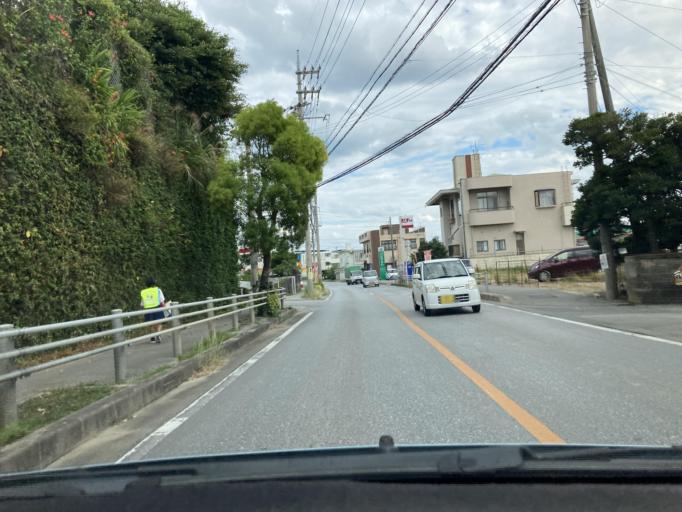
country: JP
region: Okinawa
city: Gushikawa
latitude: 26.3493
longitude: 127.8492
